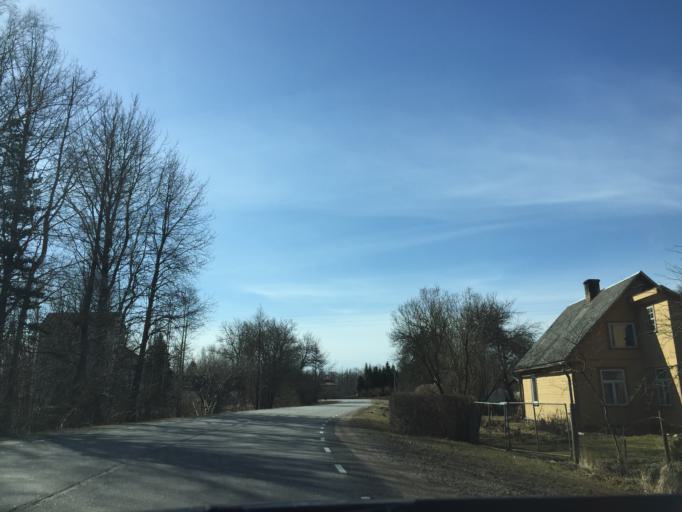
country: EE
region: Laeaene
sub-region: Lihula vald
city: Lihula
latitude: 58.6197
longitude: 23.6926
